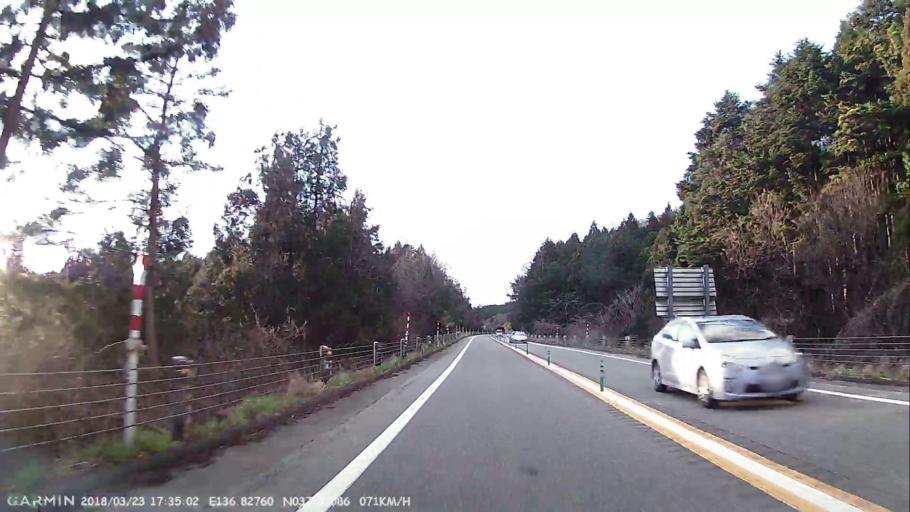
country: JP
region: Ishikawa
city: Nanao
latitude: 37.0710
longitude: 136.8275
